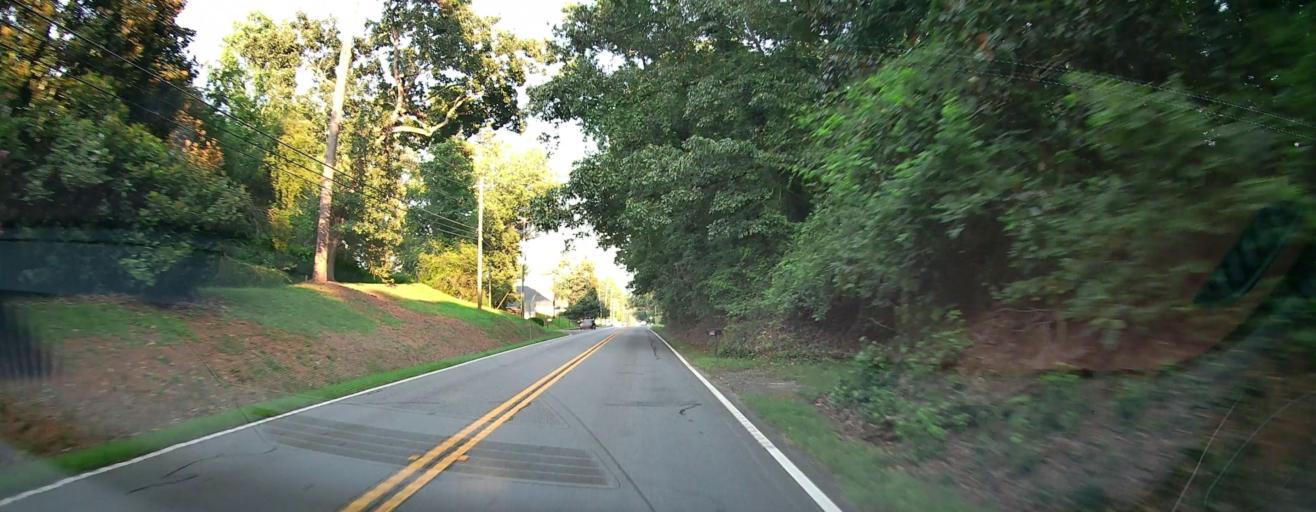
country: US
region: Georgia
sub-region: Bibb County
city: West Point
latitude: 32.8904
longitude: -83.7487
